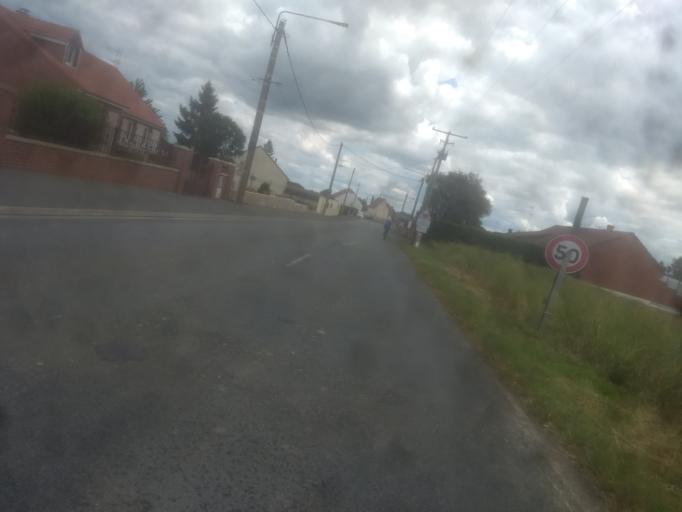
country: FR
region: Nord-Pas-de-Calais
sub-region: Departement du Pas-de-Calais
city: Agny
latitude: 50.2170
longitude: 2.7654
